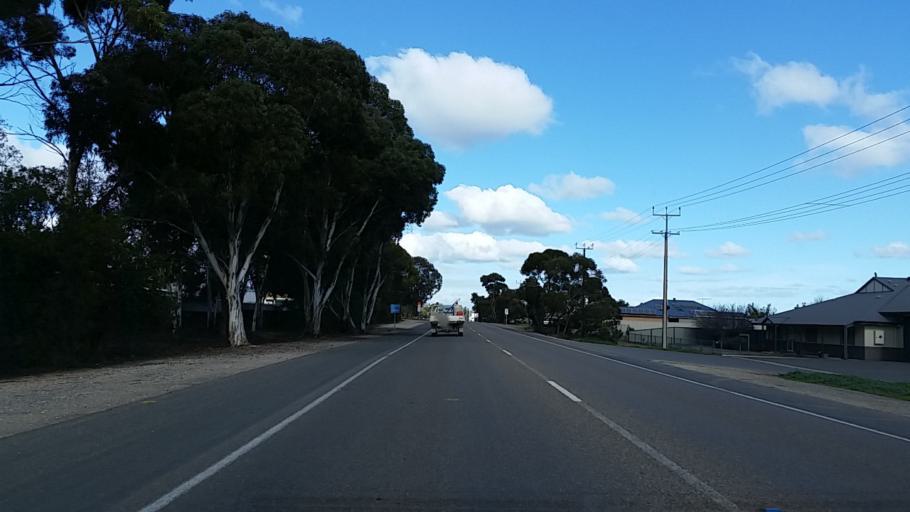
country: AU
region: South Australia
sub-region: Murray Bridge
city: Murray Bridge
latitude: -35.1441
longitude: 139.2858
